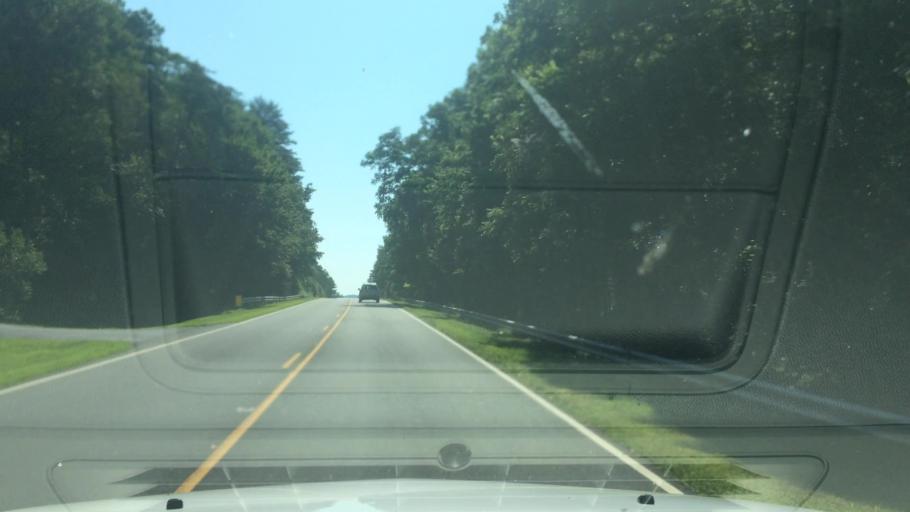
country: US
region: North Carolina
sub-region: Caldwell County
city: Hudson
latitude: 35.9090
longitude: -81.4224
